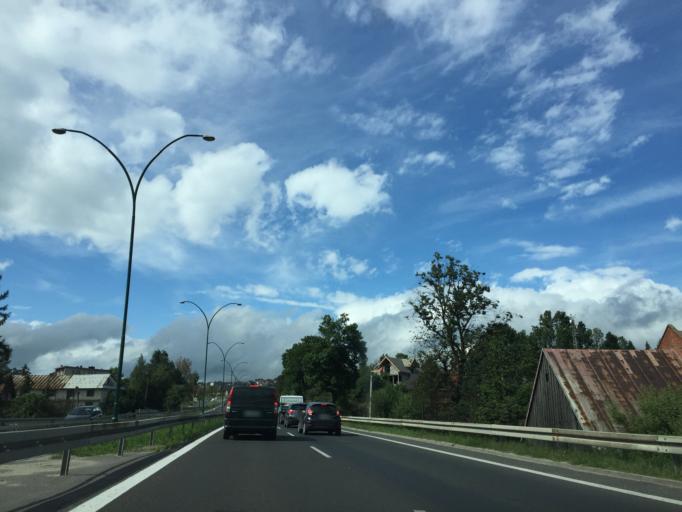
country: PL
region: Lesser Poland Voivodeship
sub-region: Powiat nowotarski
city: Nowy Targ
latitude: 49.4863
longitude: 20.0191
